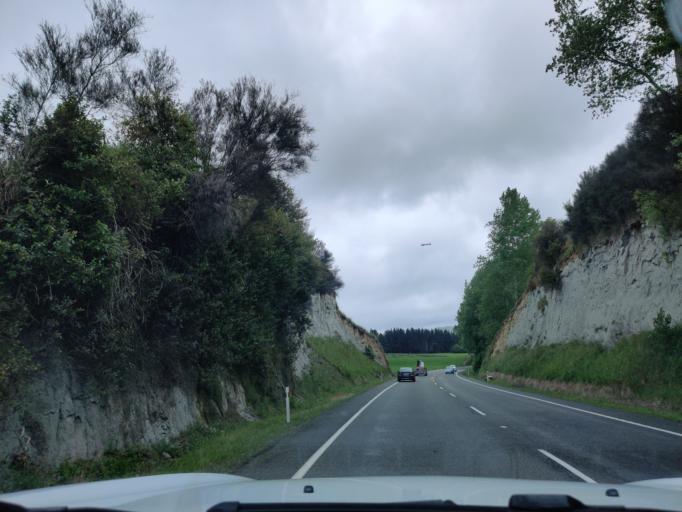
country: NZ
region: Manawatu-Wanganui
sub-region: Ruapehu District
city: Waiouru
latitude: -39.6505
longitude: 175.7693
